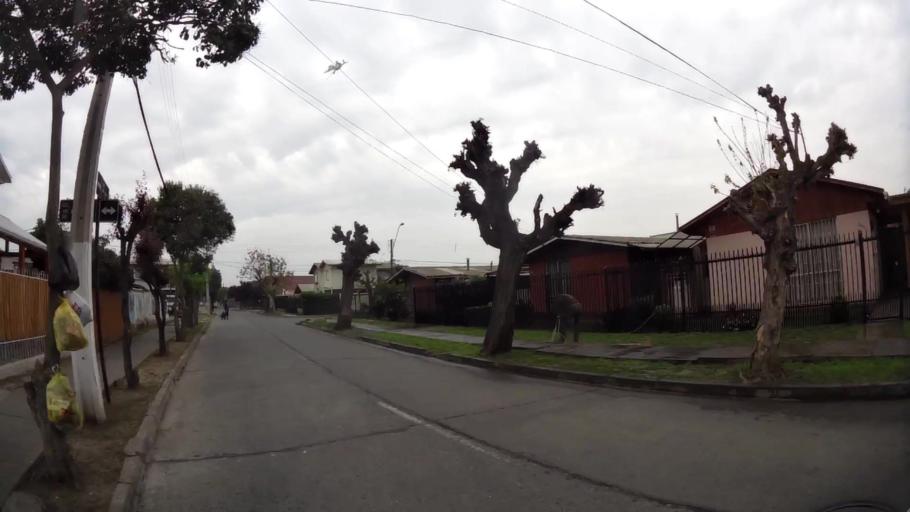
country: CL
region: Santiago Metropolitan
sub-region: Provincia de Santiago
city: Lo Prado
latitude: -33.5014
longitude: -70.7488
